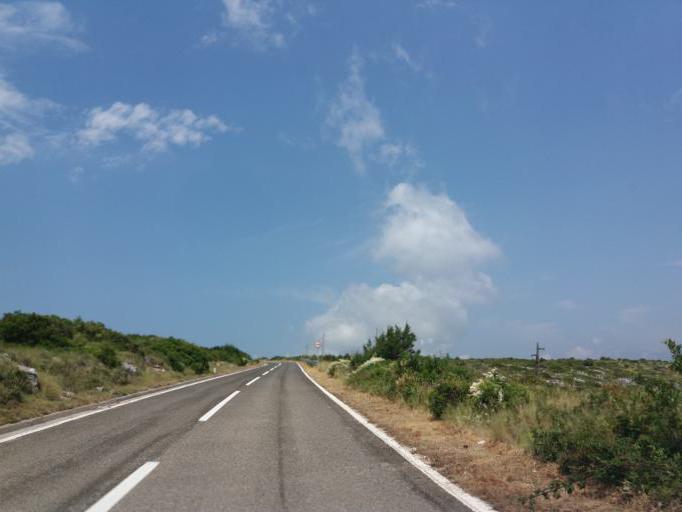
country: HR
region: Zadarska
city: Ugljan
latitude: 44.0252
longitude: 15.0327
